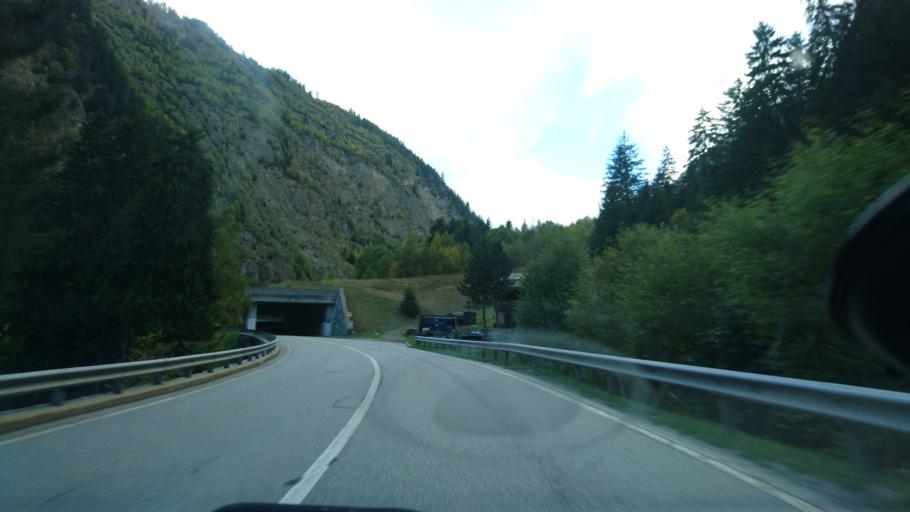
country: CH
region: Valais
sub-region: Leuk District
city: Gampel
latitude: 46.3467
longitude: 7.7572
